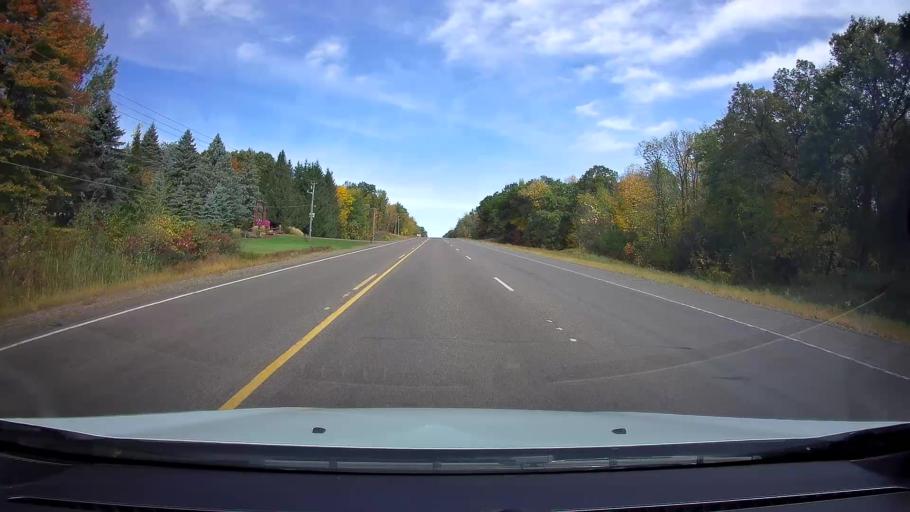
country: US
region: Wisconsin
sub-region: Polk County
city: Saint Croix Falls
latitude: 45.3700
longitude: -92.6365
